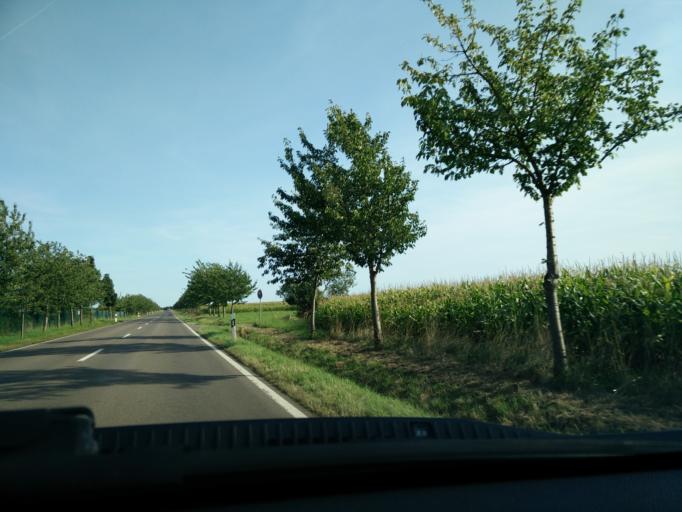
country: DE
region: Saxony
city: Bad Lausick
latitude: 51.1201
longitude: 12.6697
